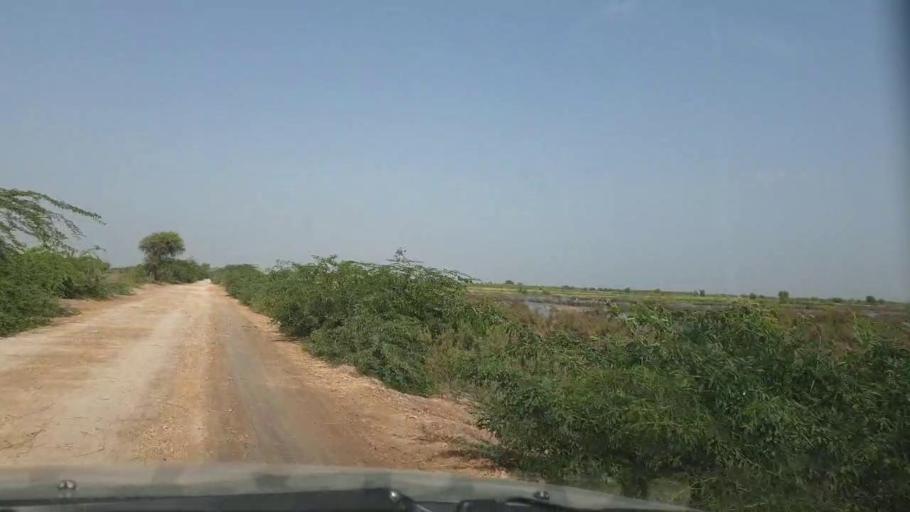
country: PK
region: Sindh
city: Tando Ghulam Ali
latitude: 25.0846
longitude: 68.8020
